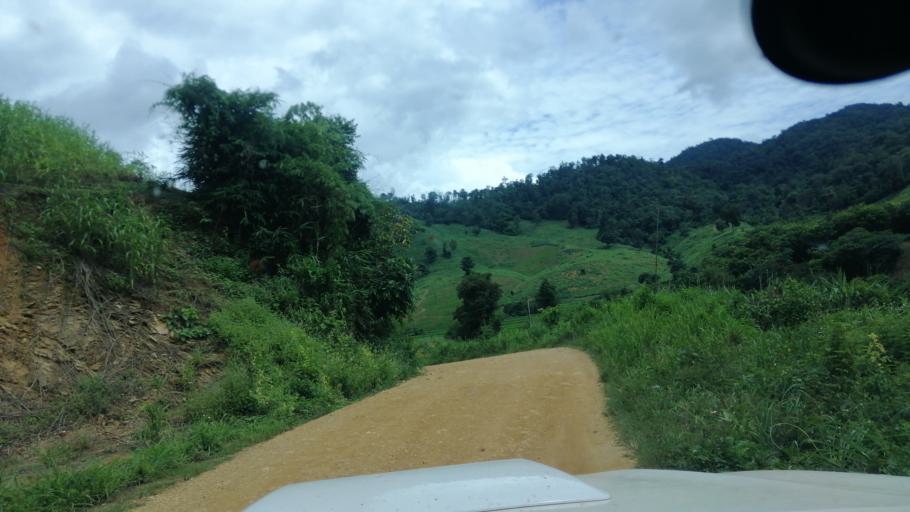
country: TH
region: Phayao
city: Phu Sang
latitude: 19.7138
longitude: 100.4878
